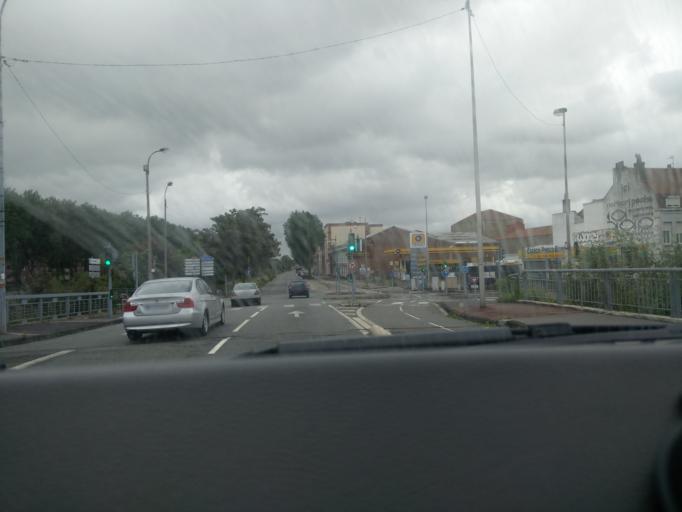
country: FR
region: Nord-Pas-de-Calais
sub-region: Departement du Nord
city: Dunkerque
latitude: 51.0297
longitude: 2.3715
